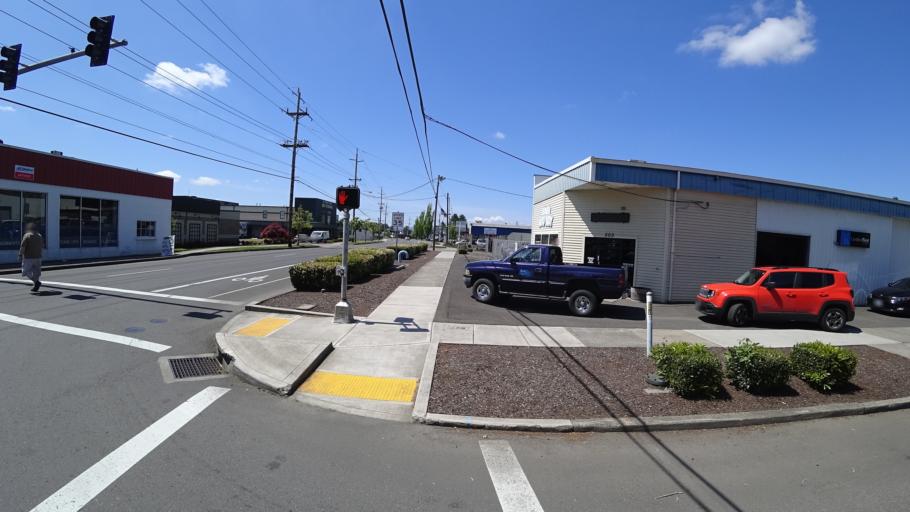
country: US
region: Oregon
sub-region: Washington County
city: Hillsboro
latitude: 45.5202
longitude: -122.9957
